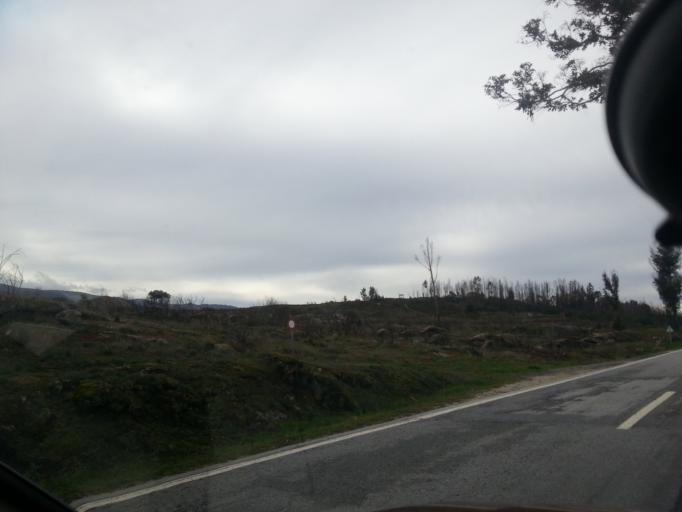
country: PT
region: Guarda
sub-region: Fornos de Algodres
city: Fornos de Algodres
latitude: 40.5249
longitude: -7.5930
